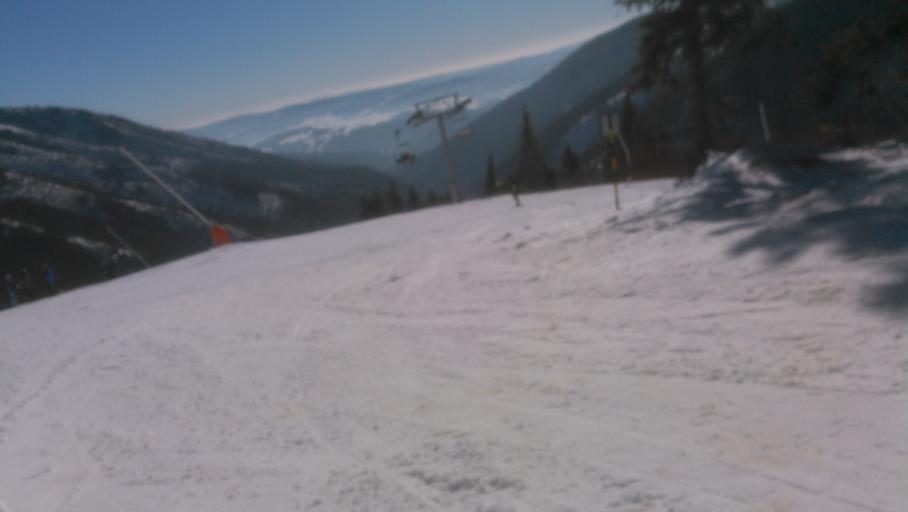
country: SK
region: Banskobystricky
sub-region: Okres Banska Bystrica
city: Brezno
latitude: 48.9290
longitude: 19.5996
